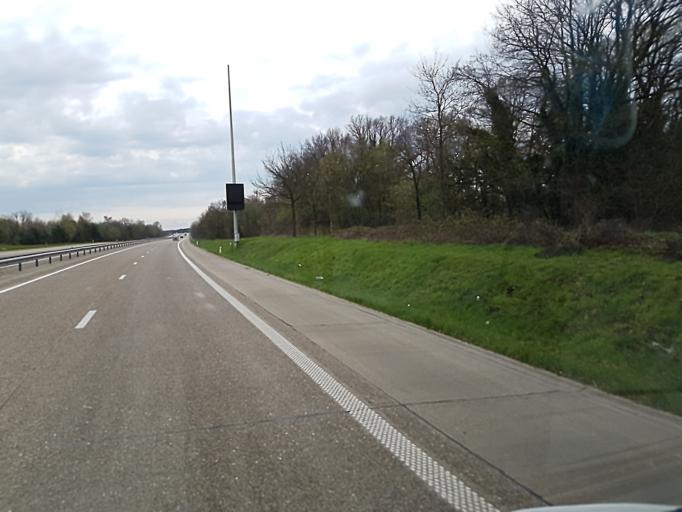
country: BE
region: Flanders
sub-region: Provincie Limburg
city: Helchteren
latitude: 51.1029
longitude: 5.3770
